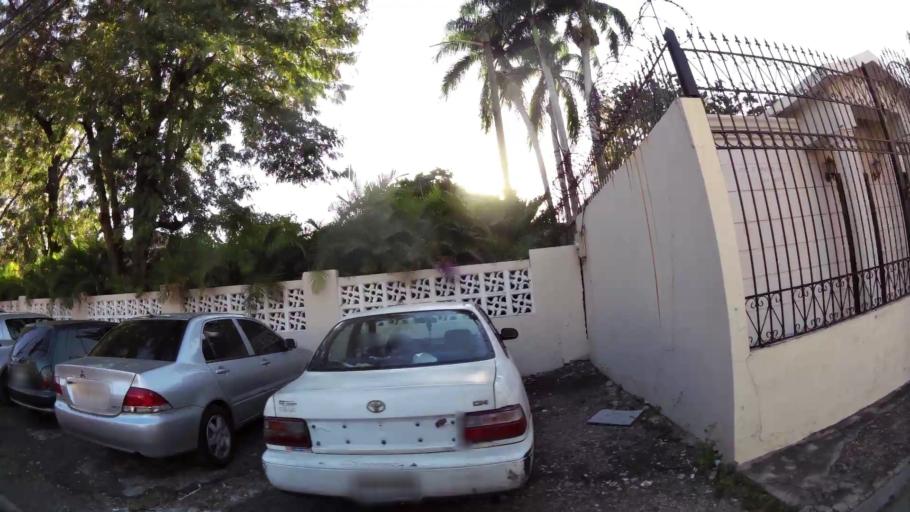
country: DO
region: Nacional
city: Santo Domingo
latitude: 18.4859
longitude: -69.9694
